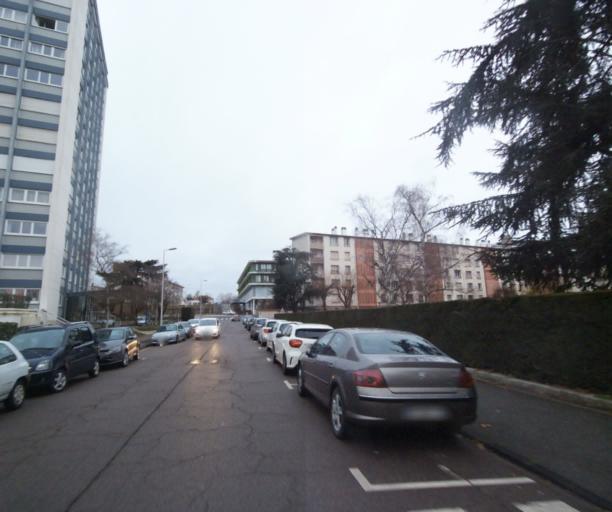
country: FR
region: Rhone-Alpes
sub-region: Departement de la Loire
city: Roanne
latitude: 46.0409
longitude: 4.0789
